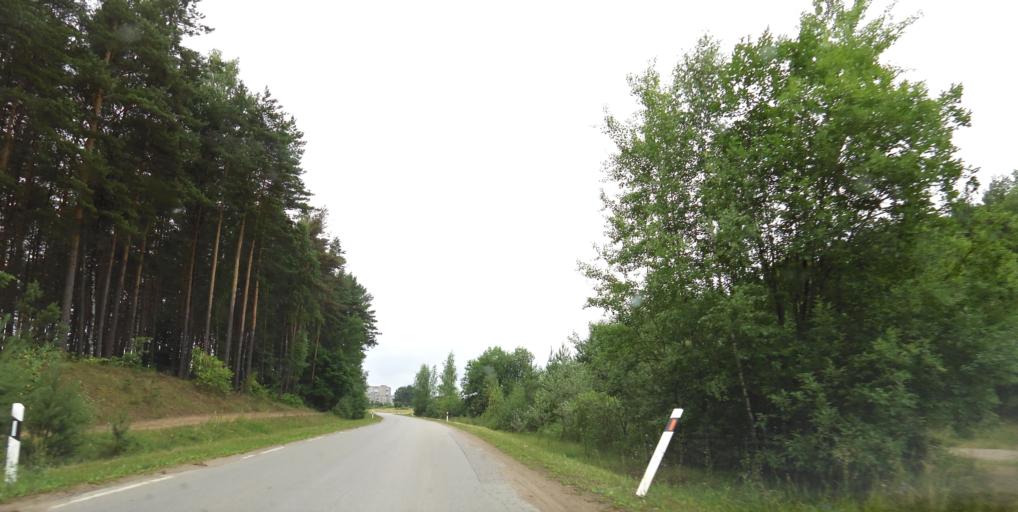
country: LT
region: Vilnius County
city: Pilaite
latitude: 54.6991
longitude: 25.1822
